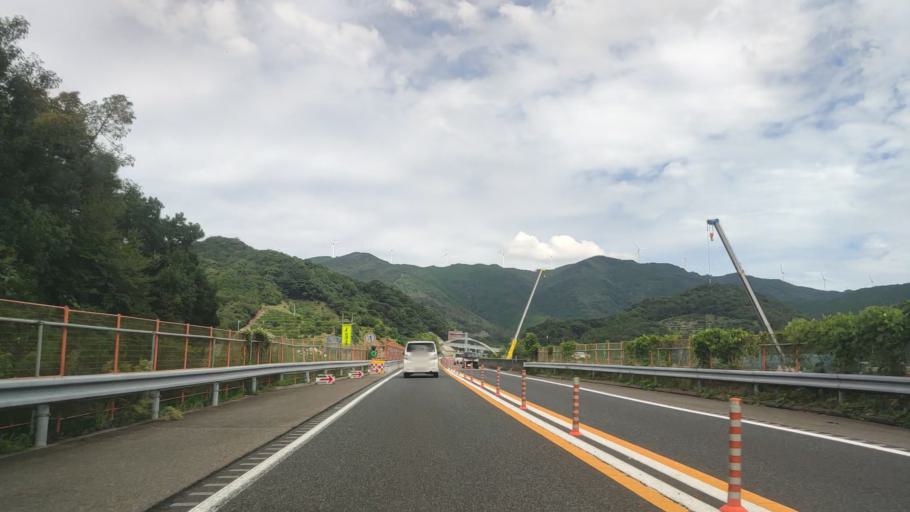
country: JP
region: Wakayama
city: Gobo
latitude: 33.9313
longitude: 135.1939
